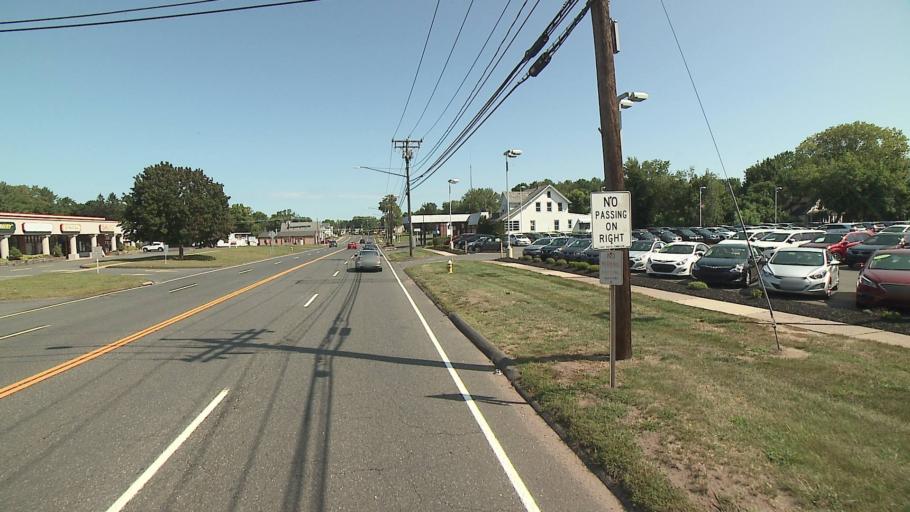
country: US
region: Connecticut
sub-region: Hartford County
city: Thompsonville
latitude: 42.0010
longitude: -72.5937
